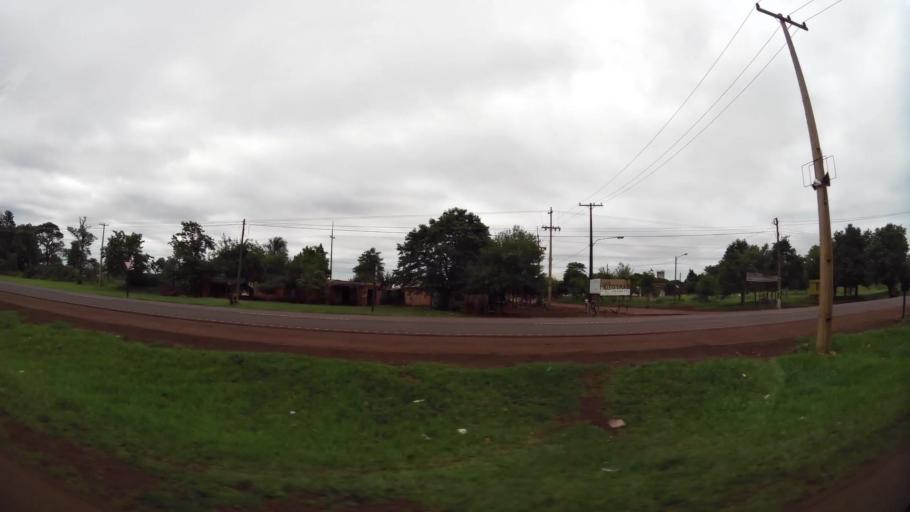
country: PY
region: Alto Parana
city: Colonia Yguazu
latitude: -25.4875
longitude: -54.8415
